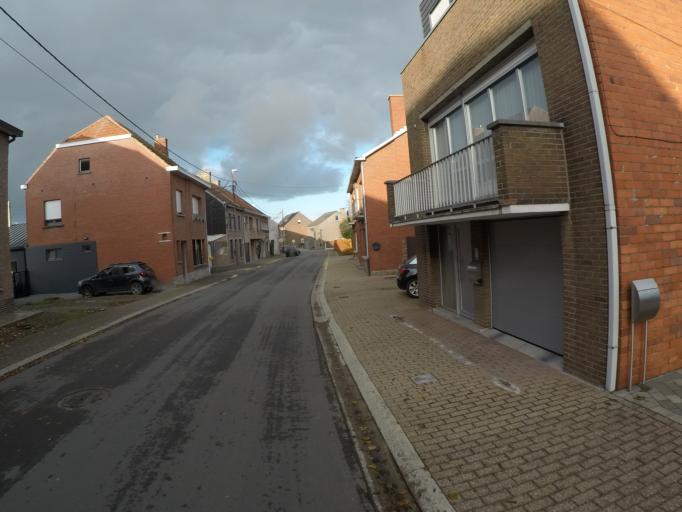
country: BE
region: Flanders
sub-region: Provincie Vlaams-Brabant
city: Opwijk
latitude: 50.9660
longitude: 4.1917
